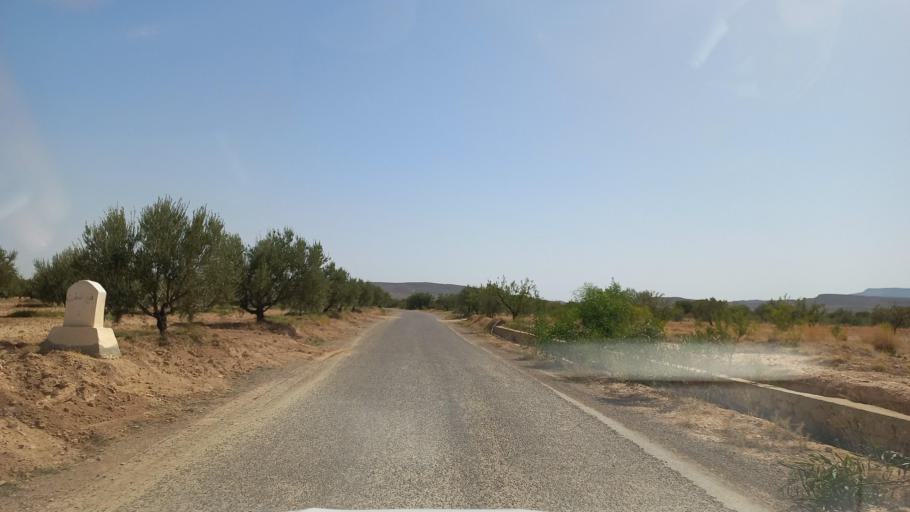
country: TN
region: Al Qasrayn
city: Kasserine
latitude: 35.2180
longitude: 9.0415
